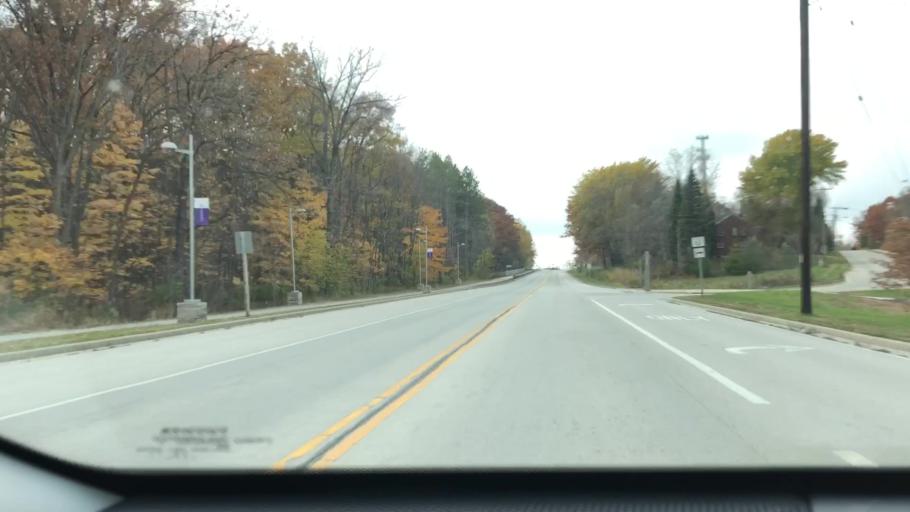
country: US
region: Wisconsin
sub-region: Brown County
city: Oneida
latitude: 44.4998
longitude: -88.1867
